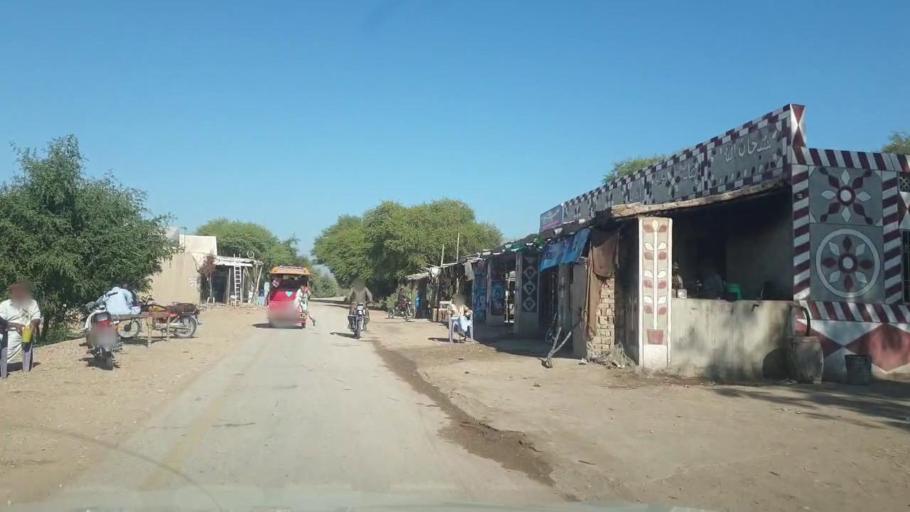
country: PK
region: Sindh
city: Bhan
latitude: 26.5477
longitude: 67.6339
